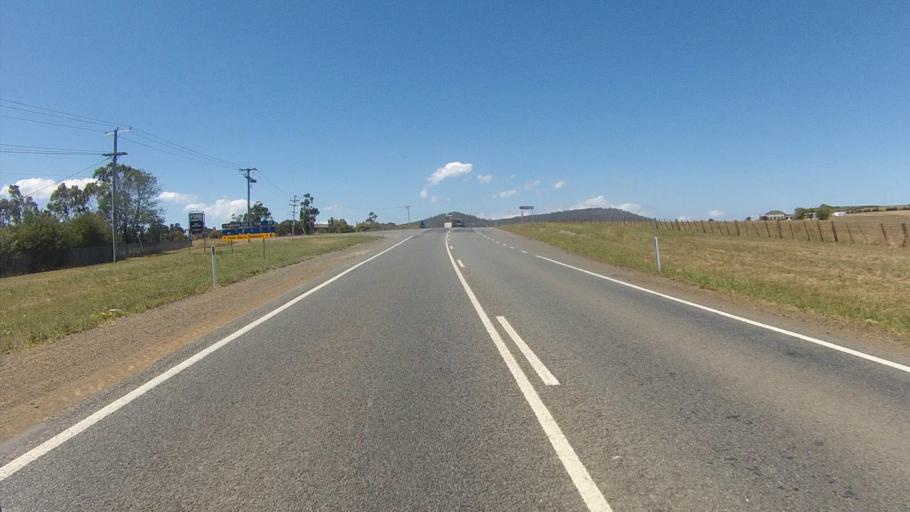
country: AU
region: Tasmania
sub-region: Sorell
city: Sorell
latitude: -42.7815
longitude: 147.5753
